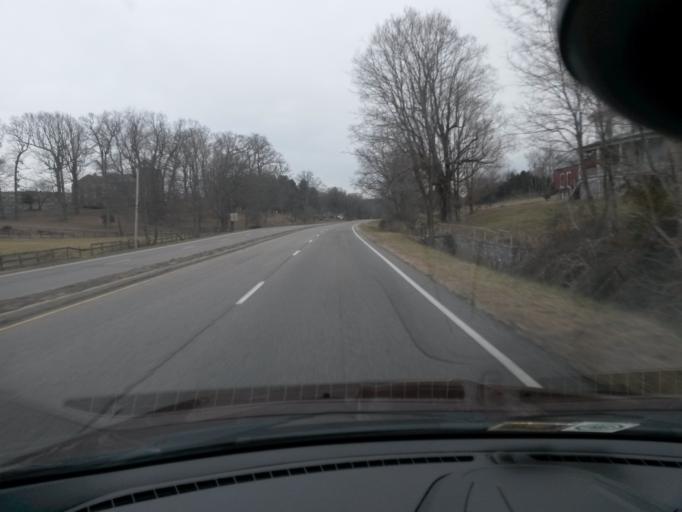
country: US
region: Virginia
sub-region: Augusta County
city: Stuarts Draft
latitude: 37.9317
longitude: -79.1971
